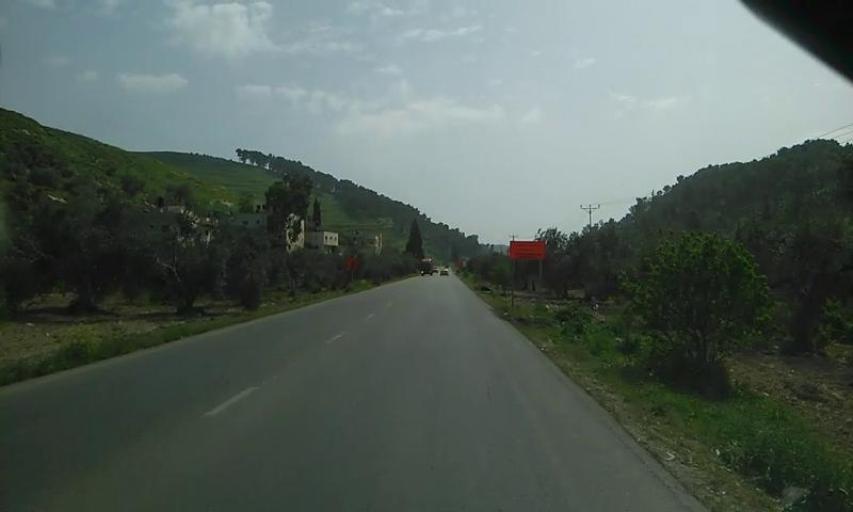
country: PS
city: Bir al Basha
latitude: 32.4057
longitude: 35.2265
